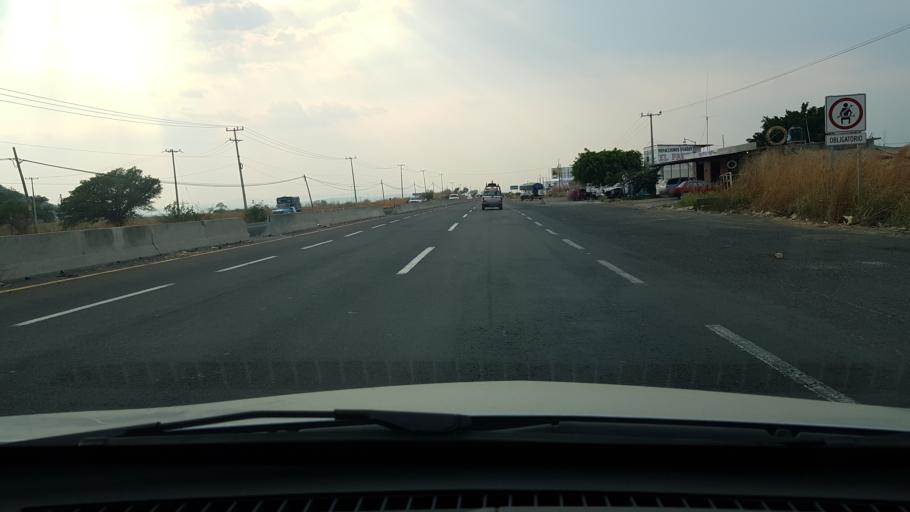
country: MX
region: Morelos
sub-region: Ayala
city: Unidad Habitacional Mariano Matamoros
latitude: 18.7528
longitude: -98.8554
